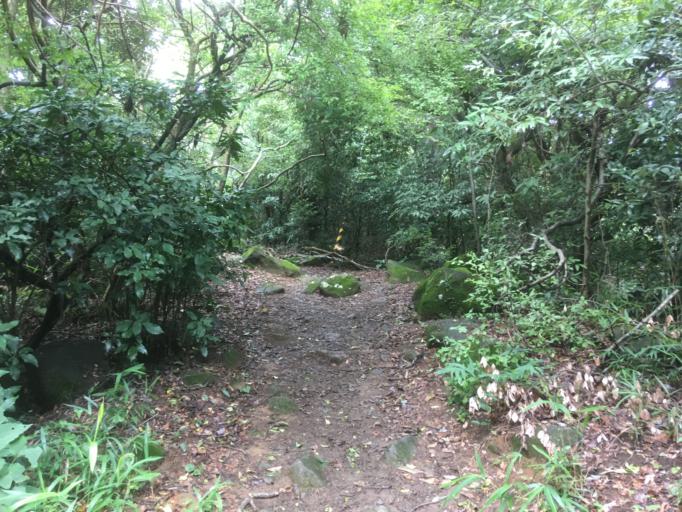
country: JP
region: Nara
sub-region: Ikoma-shi
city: Ikoma
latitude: 34.6729
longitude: 135.6754
